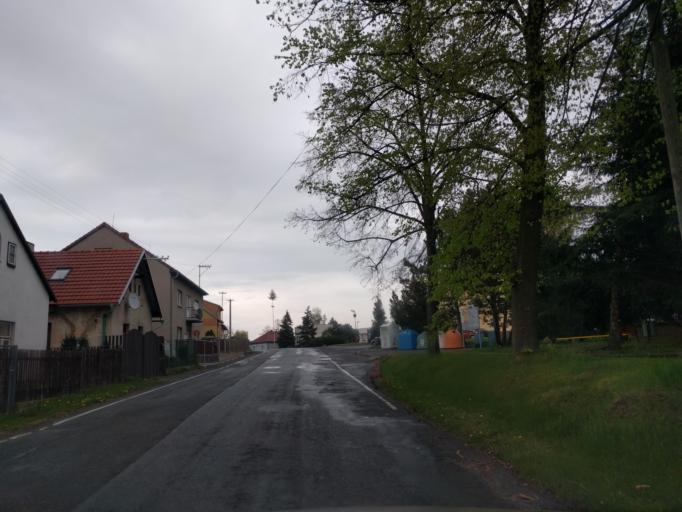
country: CZ
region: Central Bohemia
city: Dobris
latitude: 49.7036
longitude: 14.1439
